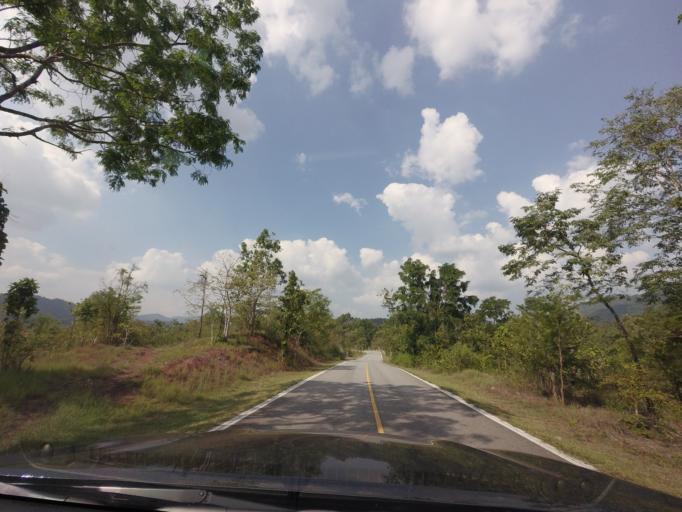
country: TH
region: Uttaradit
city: Ban Khok
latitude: 18.1770
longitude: 101.0740
